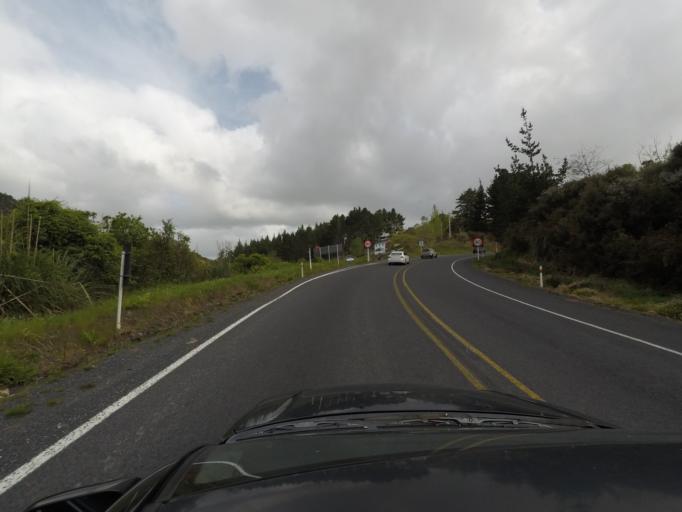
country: NZ
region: Auckland
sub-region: Auckland
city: Pakuranga
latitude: -36.9251
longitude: 174.9360
